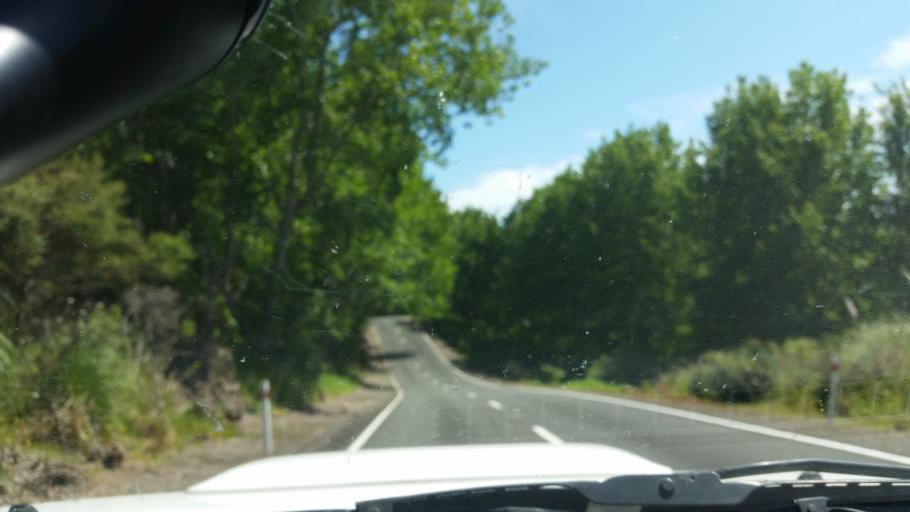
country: NZ
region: Auckland
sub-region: Auckland
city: Wellsford
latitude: -36.2119
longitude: 174.3914
